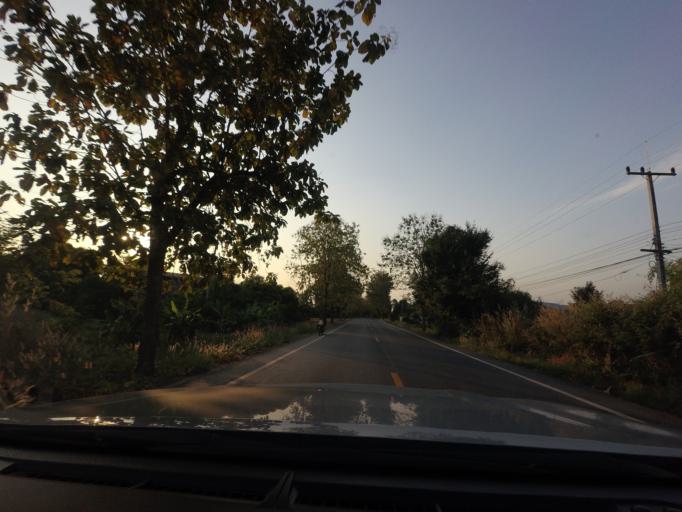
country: TH
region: Phitsanulok
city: Noen Maprang
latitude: 16.6902
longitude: 100.5269
